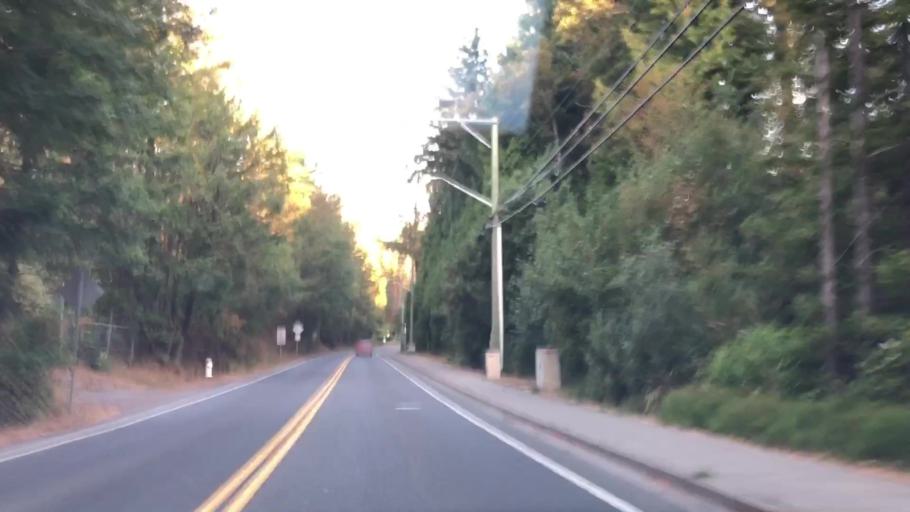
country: CA
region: British Columbia
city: Colwood
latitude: 48.4088
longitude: -123.5093
